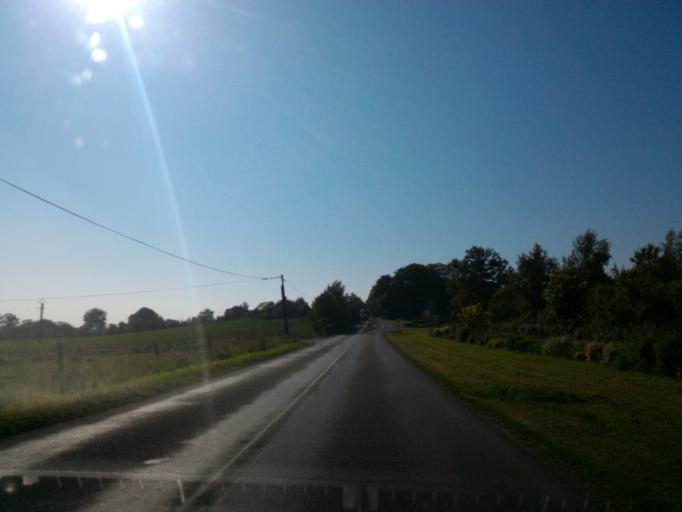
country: FR
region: Pays de la Loire
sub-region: Departement de la Mayenne
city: Juvigne
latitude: 48.2071
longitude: -1.0631
